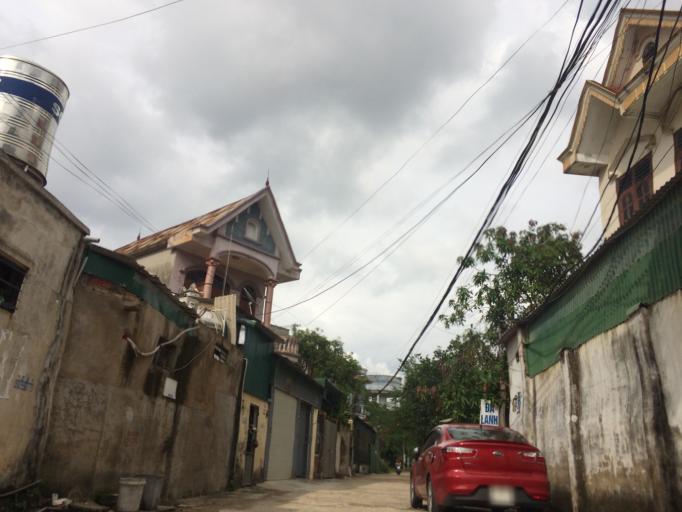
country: VN
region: Ha Tinh
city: Ha Tinh
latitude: 18.3246
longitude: 105.9139
